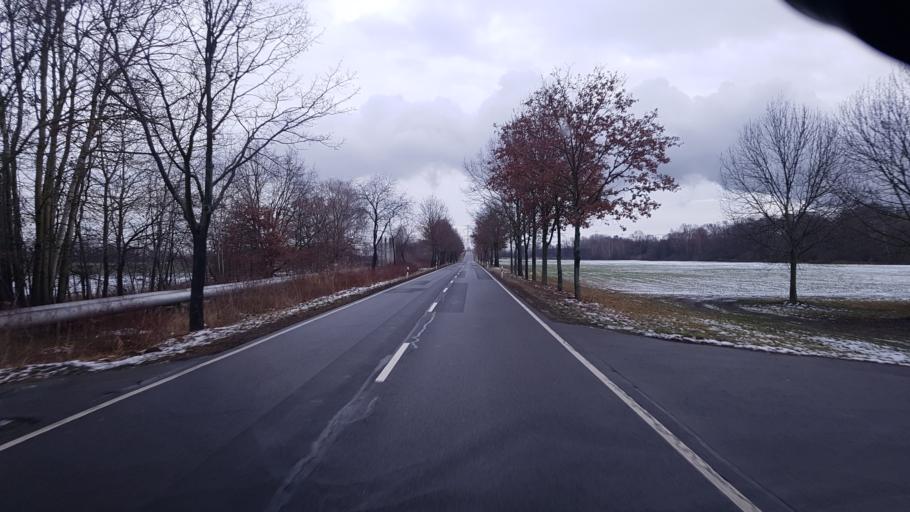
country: DE
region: Brandenburg
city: Peitz
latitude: 51.8512
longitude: 14.4418
